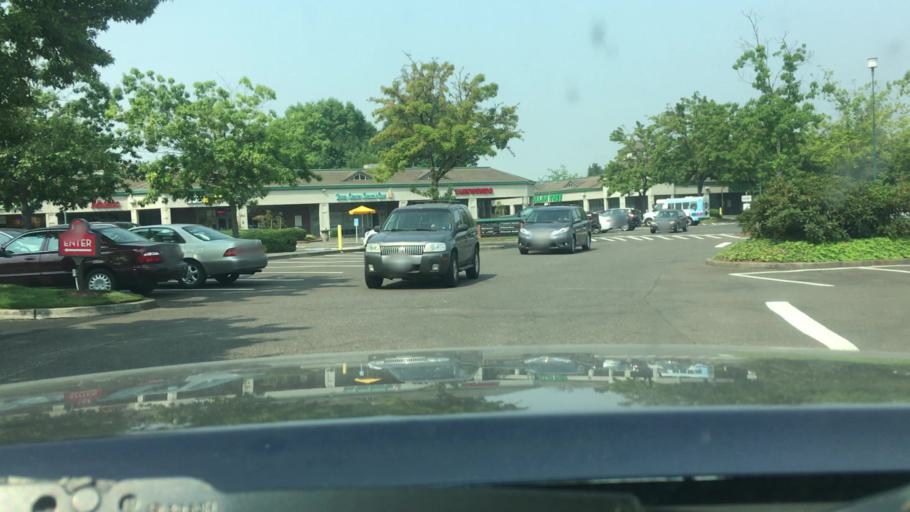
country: US
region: Oregon
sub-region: Clackamas County
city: Wilsonville
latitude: 45.3035
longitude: -122.7631
